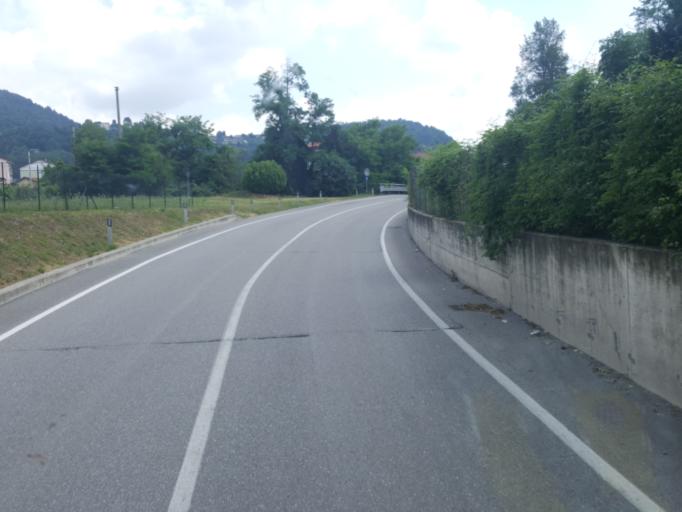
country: IT
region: Lombardy
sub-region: Provincia di Lecco
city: Calolziocorte
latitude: 45.7861
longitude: 9.4410
